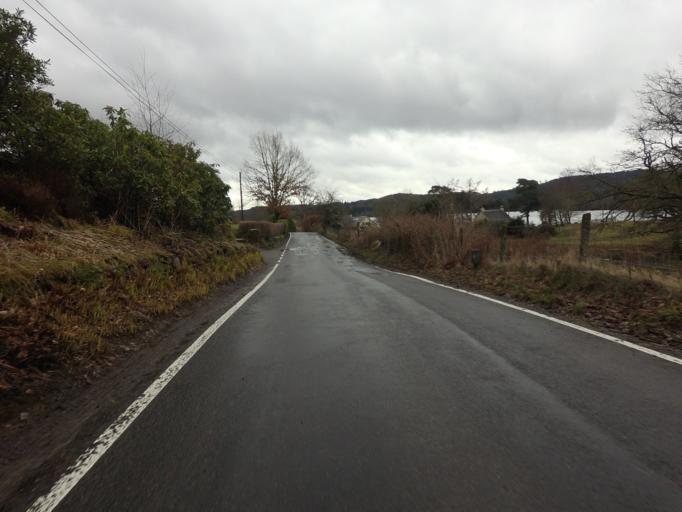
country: GB
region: Scotland
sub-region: Stirling
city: Killearn
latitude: 56.1887
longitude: -4.4934
